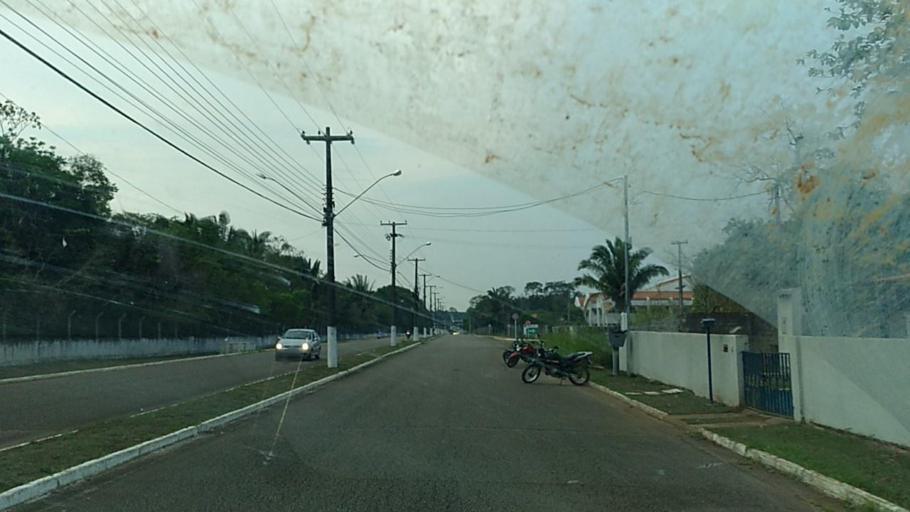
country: BR
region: Rondonia
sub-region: Porto Velho
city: Porto Velho
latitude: -8.7127
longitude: -63.8970
